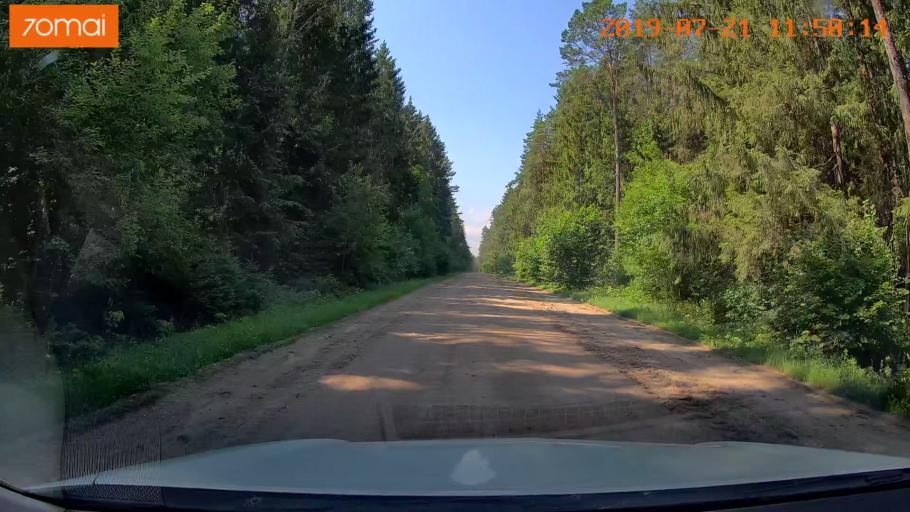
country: BY
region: Grodnenskaya
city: Lyubcha
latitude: 53.8883
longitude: 26.0288
